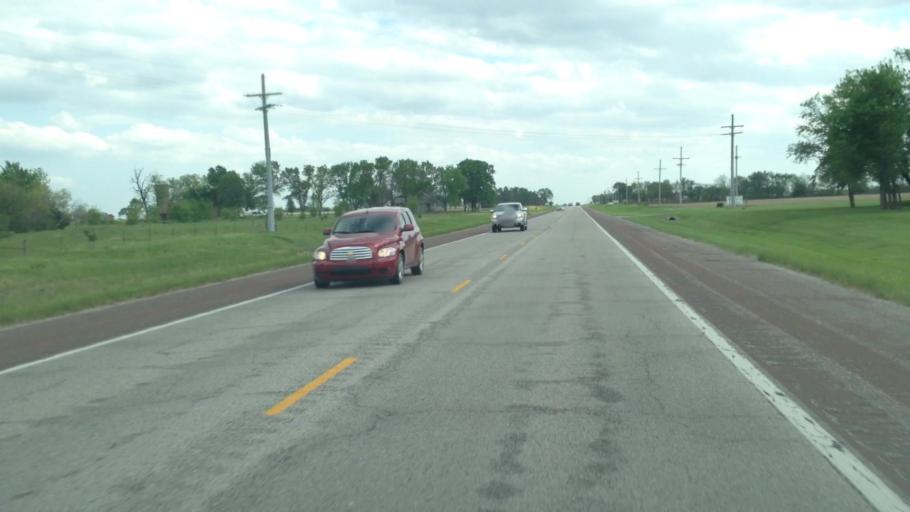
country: US
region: Kansas
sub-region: Franklin County
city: Ottawa
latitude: 38.5489
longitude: -95.2678
